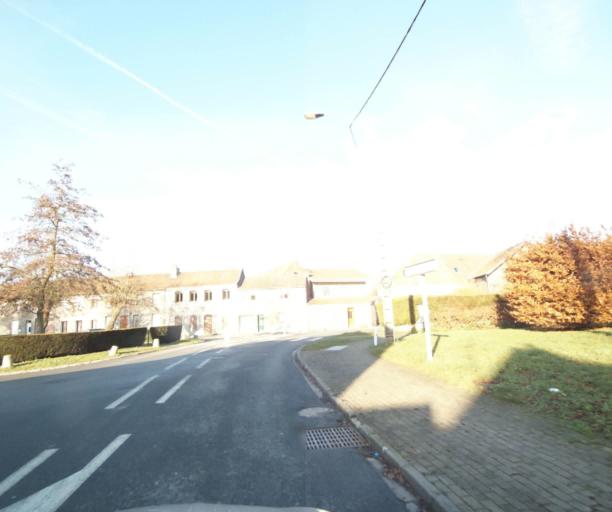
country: FR
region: Nord-Pas-de-Calais
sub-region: Departement du Nord
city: Saultain
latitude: 50.3401
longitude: 3.5775
